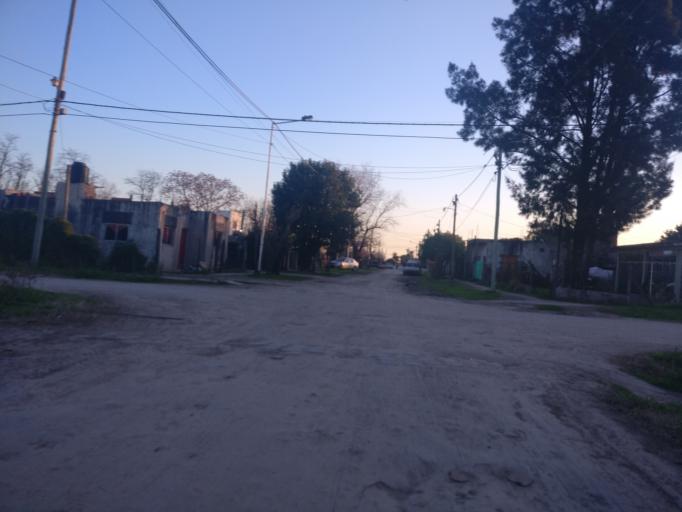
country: AR
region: Buenos Aires
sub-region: Partido de Ezeiza
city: Ezeiza
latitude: -34.9435
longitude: -58.6113
